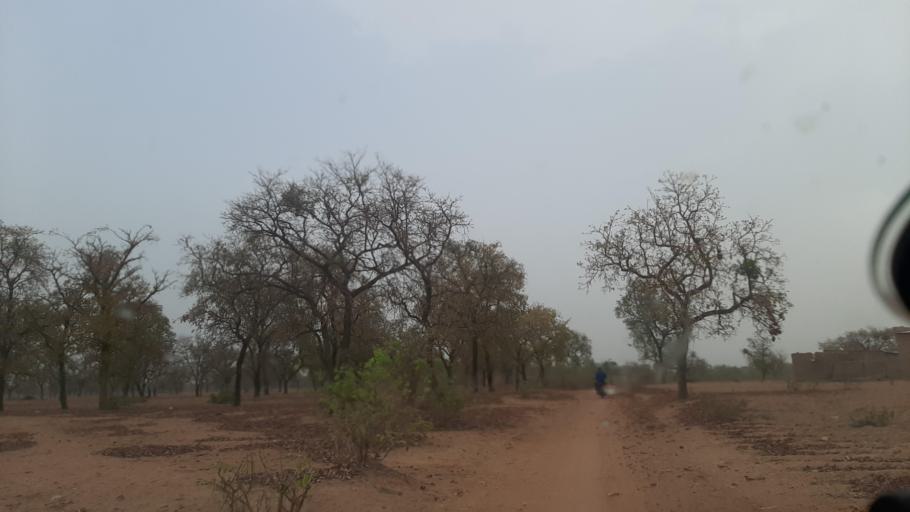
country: BF
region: Boucle du Mouhoun
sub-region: Province des Banwa
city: Salanso
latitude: 11.8669
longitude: -4.4442
